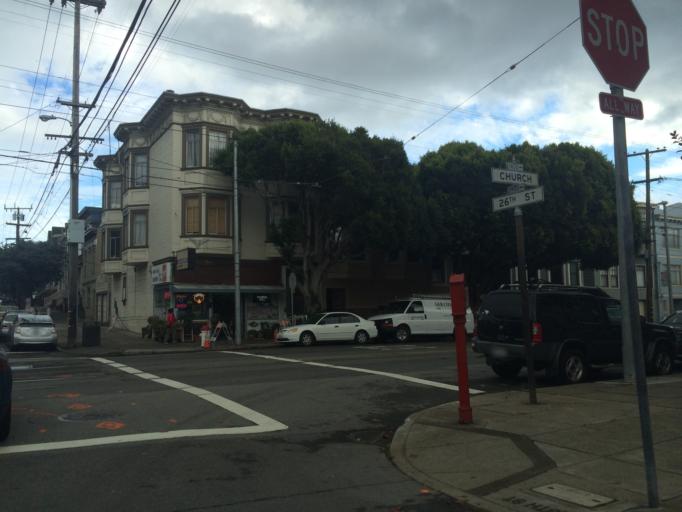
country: US
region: California
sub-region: San Francisco County
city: San Francisco
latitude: 37.7485
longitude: -122.4274
